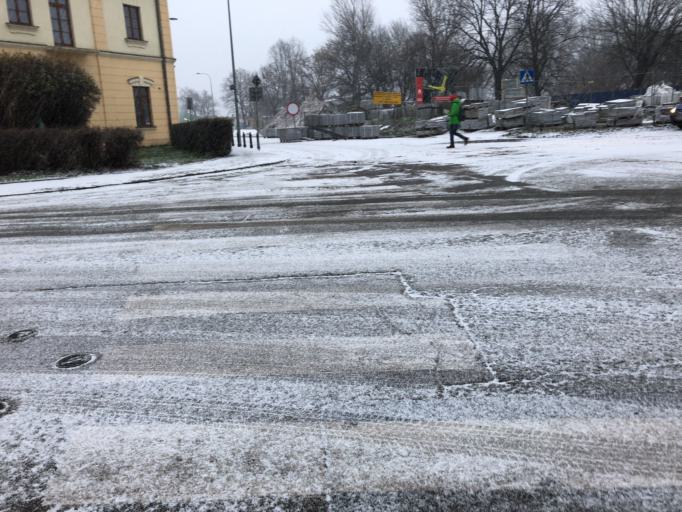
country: PL
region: Masovian Voivodeship
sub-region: Warszawa
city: Praga Polnoc
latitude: 52.2483
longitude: 21.0399
